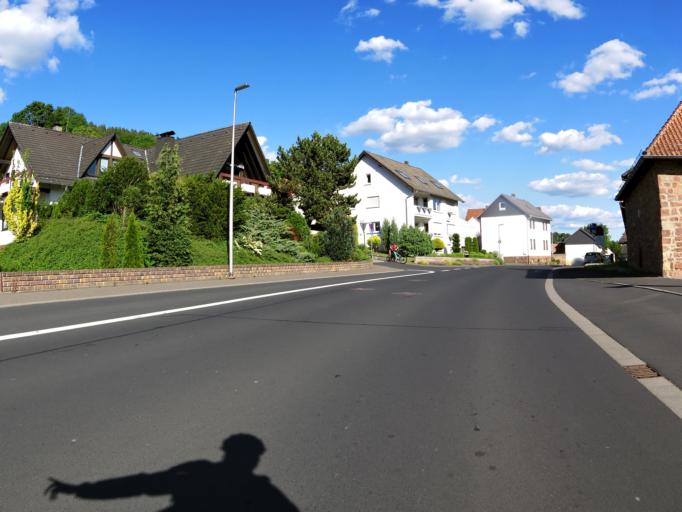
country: DE
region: Hesse
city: Philippsthal
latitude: 50.8423
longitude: 10.0052
